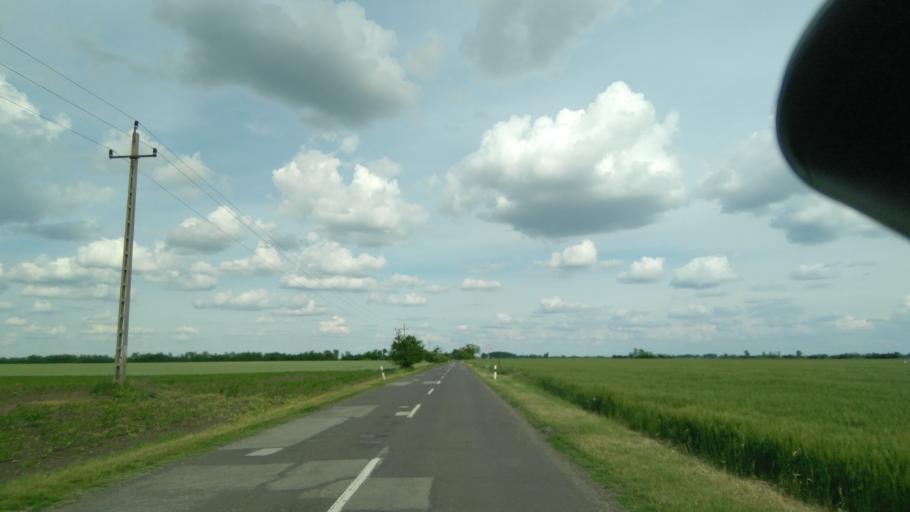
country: RO
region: Arad
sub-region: Comuna Peregu Mare
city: Peregu Mic
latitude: 46.2982
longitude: 20.9471
